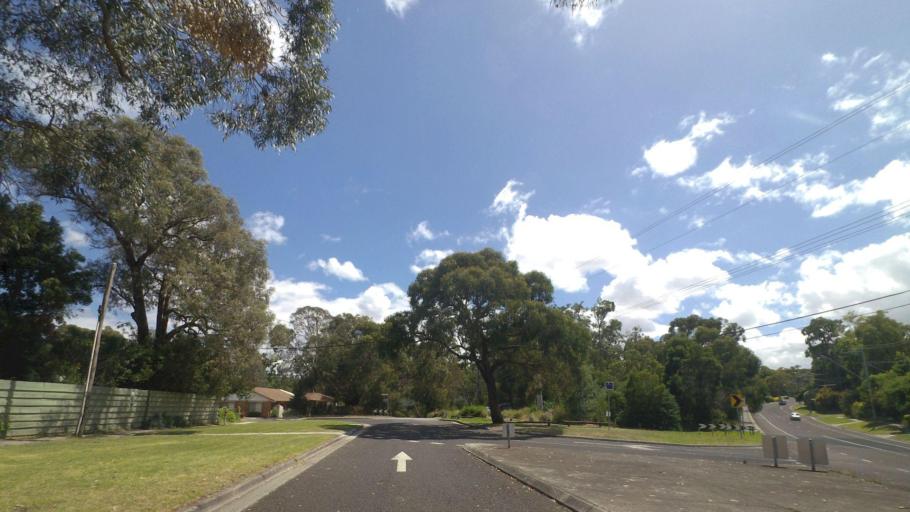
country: AU
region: Victoria
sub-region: Knox
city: Ferntree Gully
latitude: -37.8714
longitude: 145.2969
